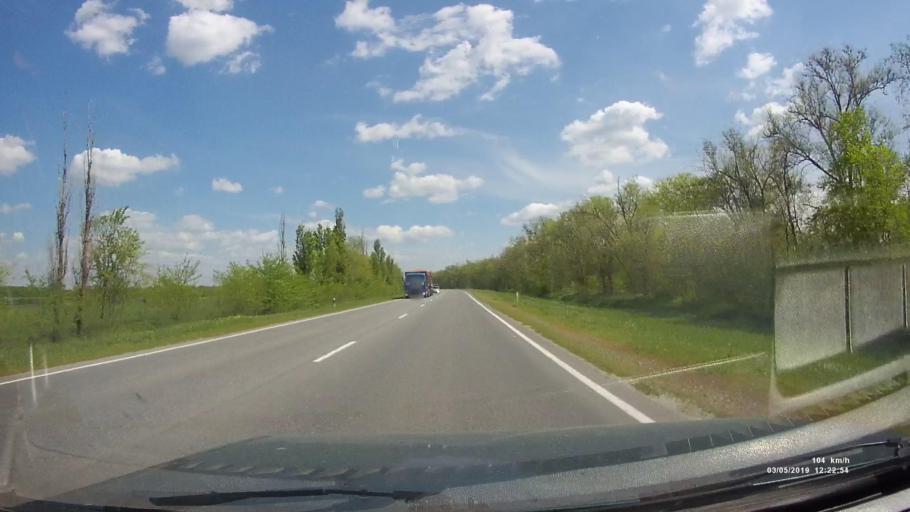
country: RU
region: Rostov
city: Semikarakorsk
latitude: 47.4066
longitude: 40.6718
